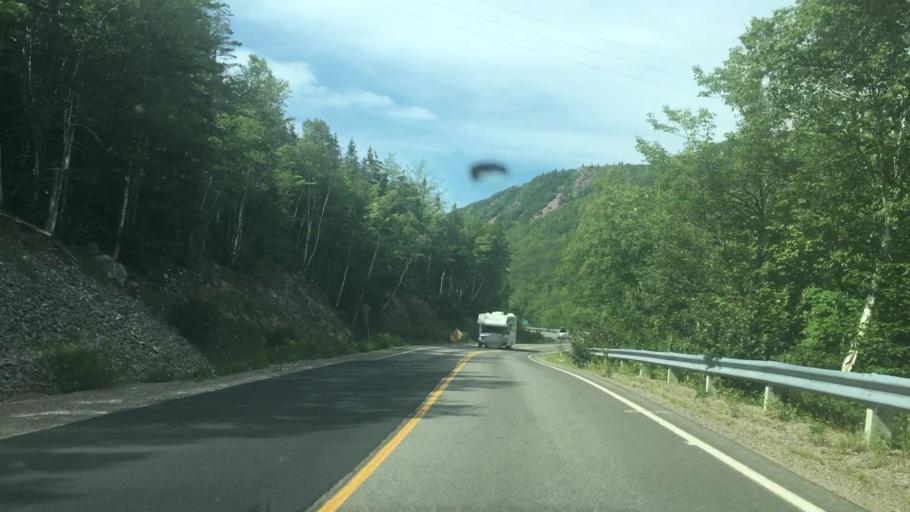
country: CA
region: Nova Scotia
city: Sydney Mines
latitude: 46.5802
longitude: -60.3906
